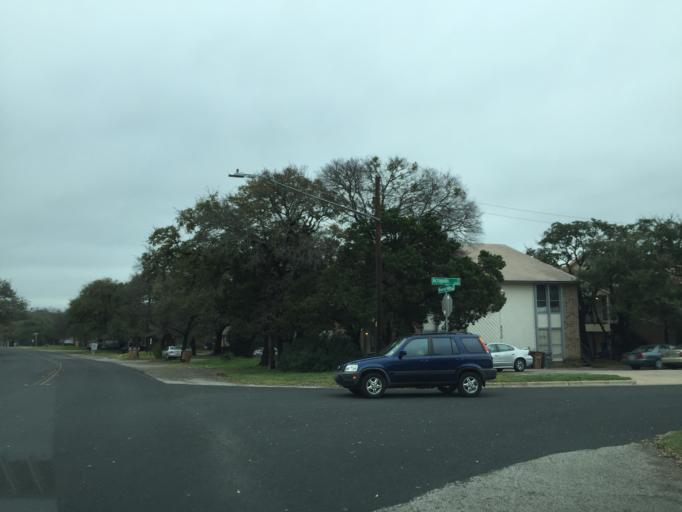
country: US
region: Texas
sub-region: Williamson County
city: Jollyville
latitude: 30.4131
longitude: -97.7311
